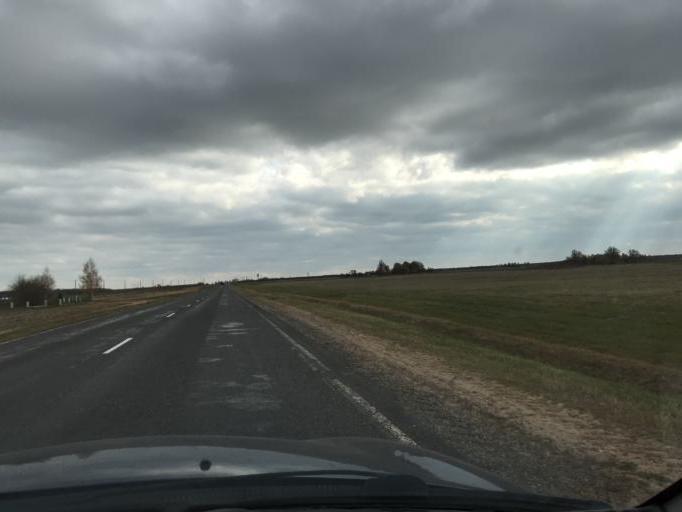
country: BY
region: Grodnenskaya
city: Lida
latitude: 53.8061
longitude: 25.1178
